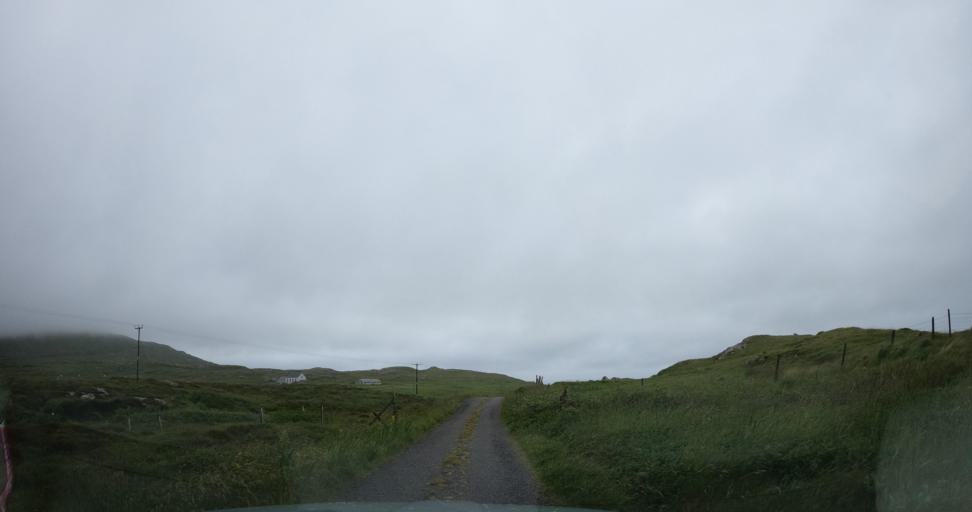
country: GB
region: Scotland
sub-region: Eilean Siar
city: Barra
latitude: 57.0031
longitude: -7.4809
